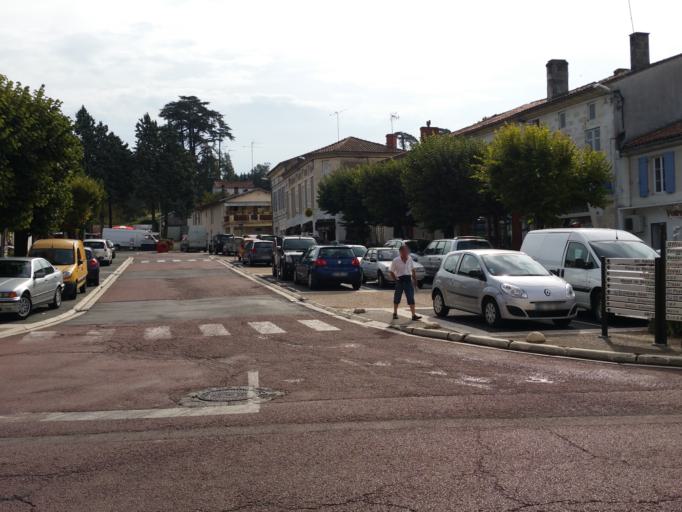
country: FR
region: Poitou-Charentes
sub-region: Departement de la Charente-Maritime
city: Mirambeau
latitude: 45.3740
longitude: -0.5707
